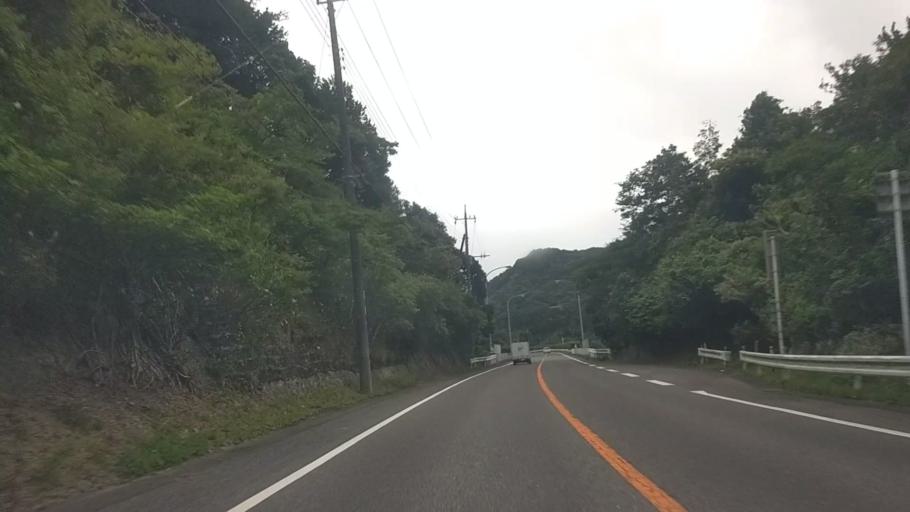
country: JP
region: Chiba
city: Kawaguchi
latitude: 35.1476
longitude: 140.0688
